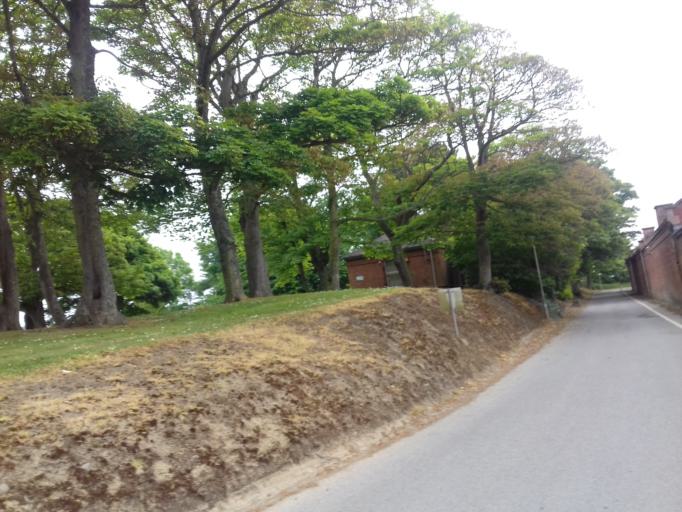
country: IE
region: Leinster
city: Portraine
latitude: 53.4873
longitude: -6.1118
